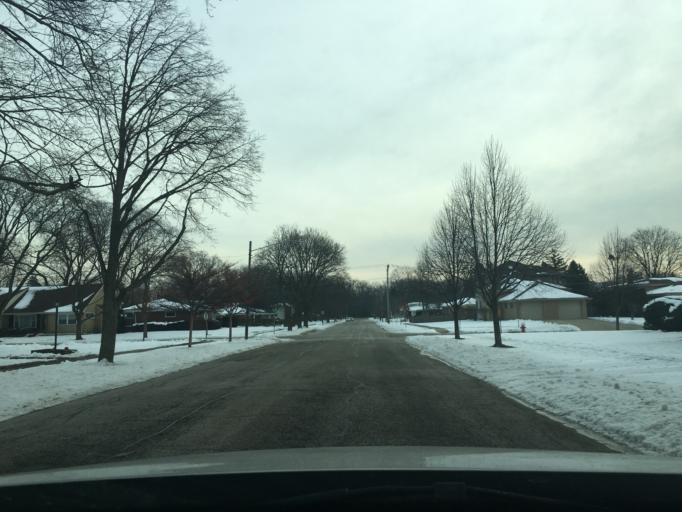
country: US
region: Illinois
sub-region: Cook County
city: Des Plaines
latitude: 42.0207
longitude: -87.8790
